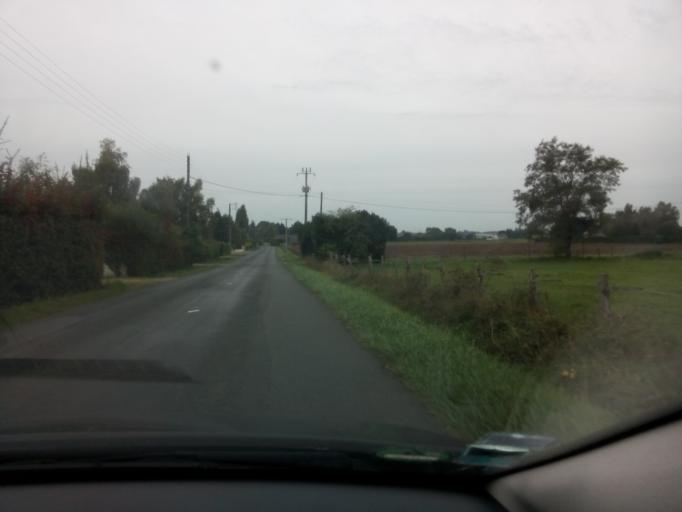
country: FR
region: Pays de la Loire
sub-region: Departement de Maine-et-Loire
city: Corne
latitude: 47.4845
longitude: -0.3382
